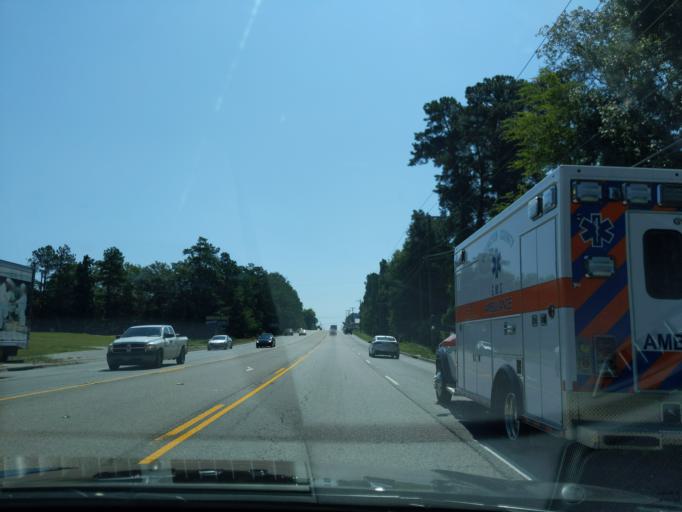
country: US
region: South Carolina
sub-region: Lexington County
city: Oak Grove
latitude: 33.9769
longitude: -81.1860
